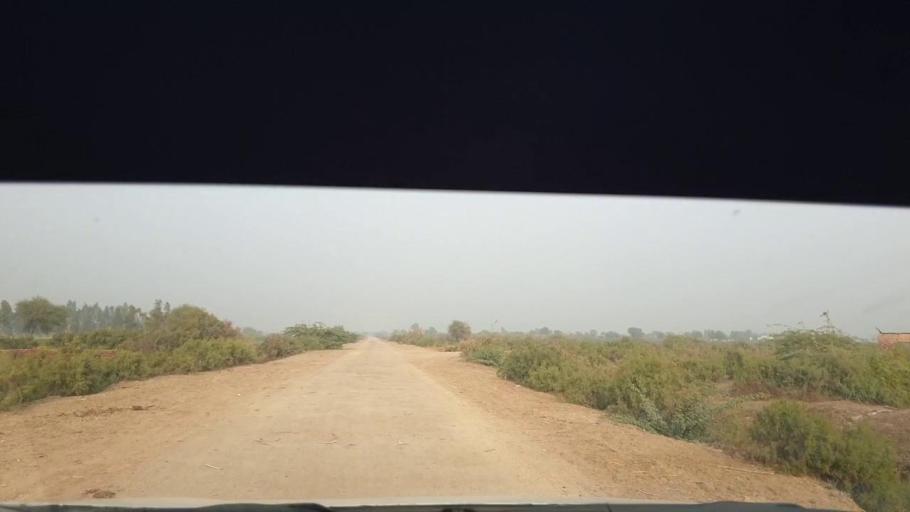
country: PK
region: Sindh
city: Berani
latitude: 25.8134
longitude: 68.8820
